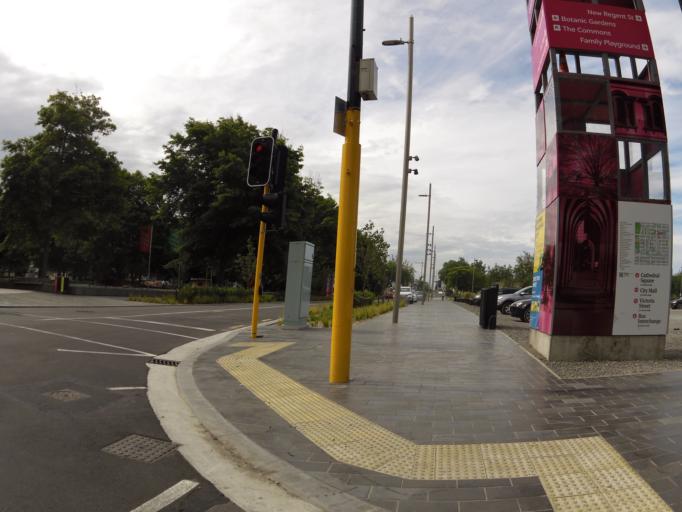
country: NZ
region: Canterbury
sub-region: Christchurch City
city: Christchurch
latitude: -43.5286
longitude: 172.6365
